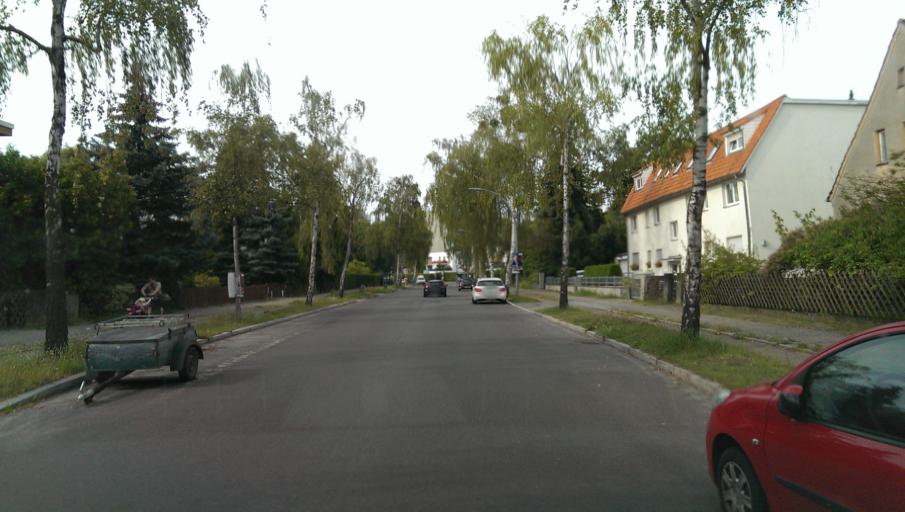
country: DE
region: Berlin
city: Zehlendorf Bezirk
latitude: 52.4173
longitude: 13.2506
